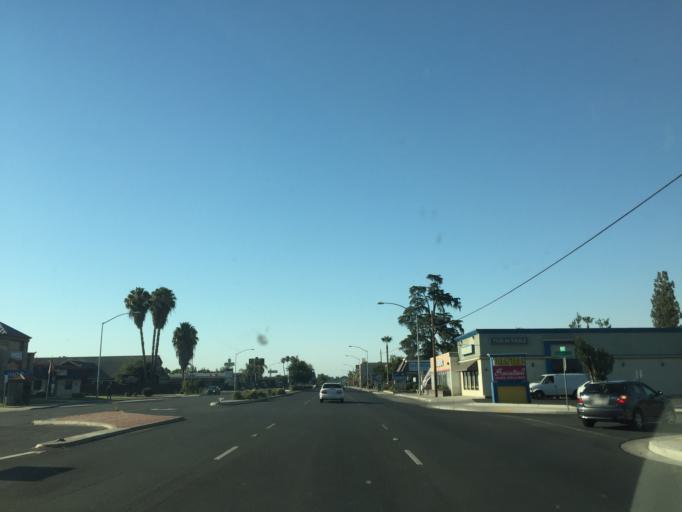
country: US
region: California
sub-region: Tulare County
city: Visalia
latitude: 36.3152
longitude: -119.3138
